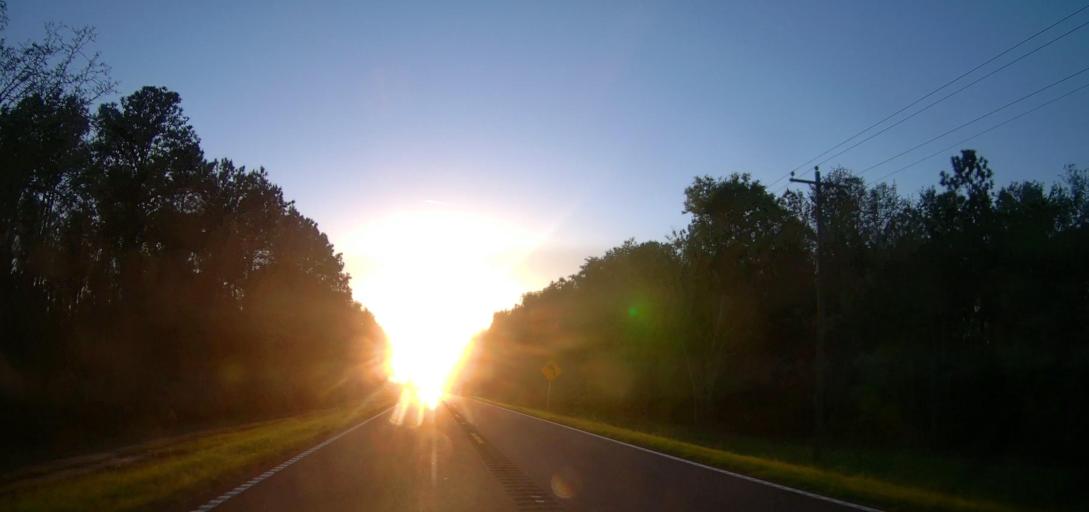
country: US
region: Georgia
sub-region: Marion County
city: Buena Vista
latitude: 32.4425
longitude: -84.6126
